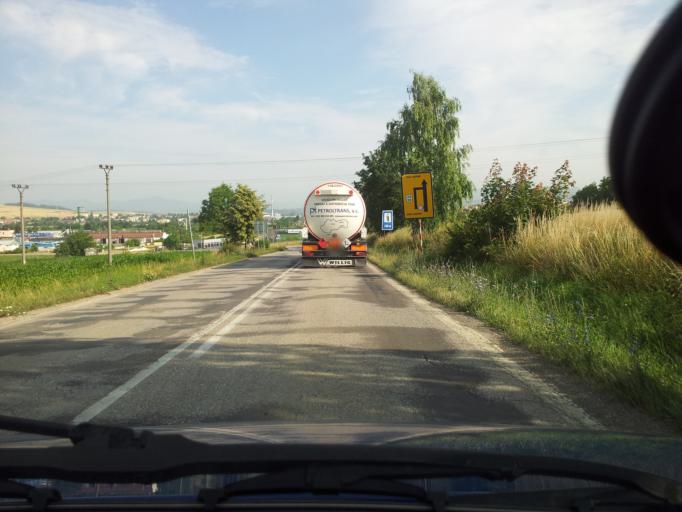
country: SK
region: Nitriansky
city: Banovce nad Bebravou
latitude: 48.7092
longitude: 18.2568
